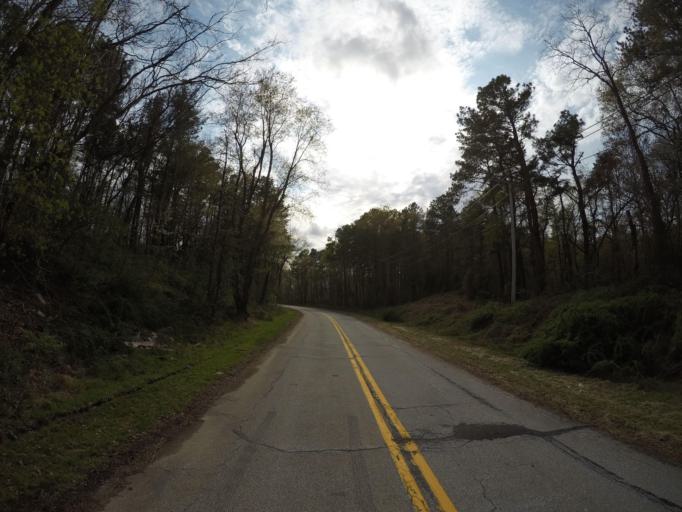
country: US
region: Delaware
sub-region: New Castle County
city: Glasgow
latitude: 39.5456
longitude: -75.7241
